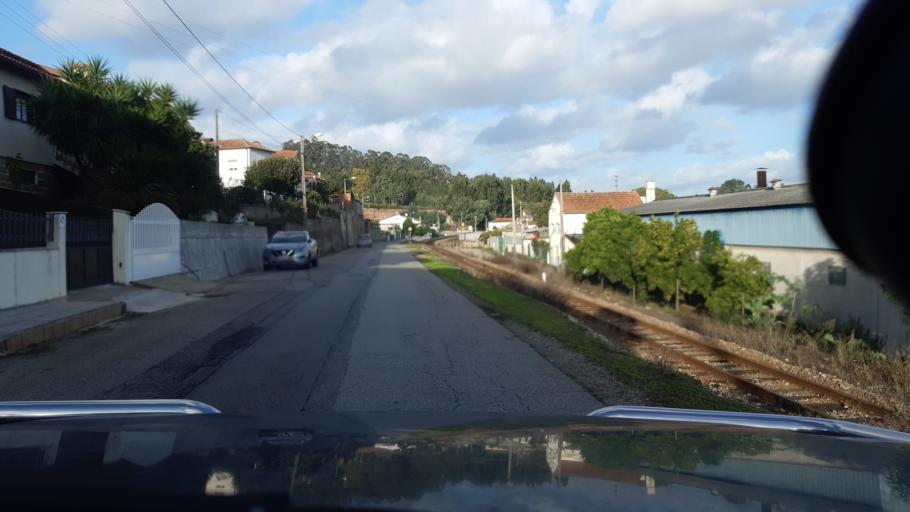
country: PT
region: Aveiro
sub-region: Agueda
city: Agueda
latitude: 40.5741
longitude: -8.4686
